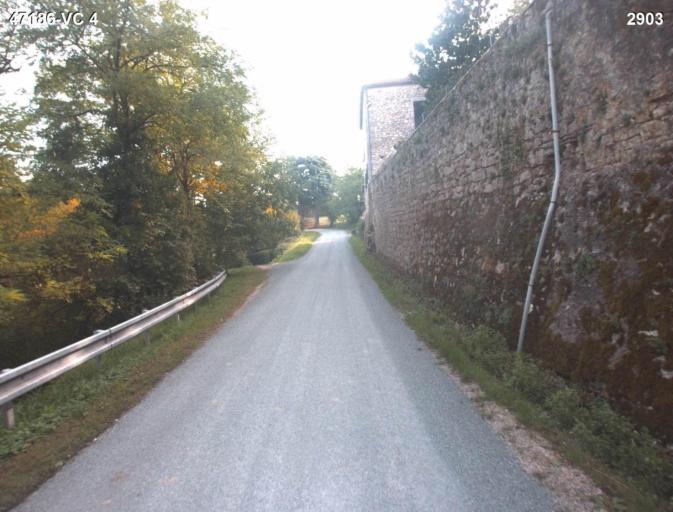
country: FR
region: Aquitaine
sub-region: Departement du Lot-et-Garonne
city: Port-Sainte-Marie
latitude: 44.2024
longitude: 0.4405
